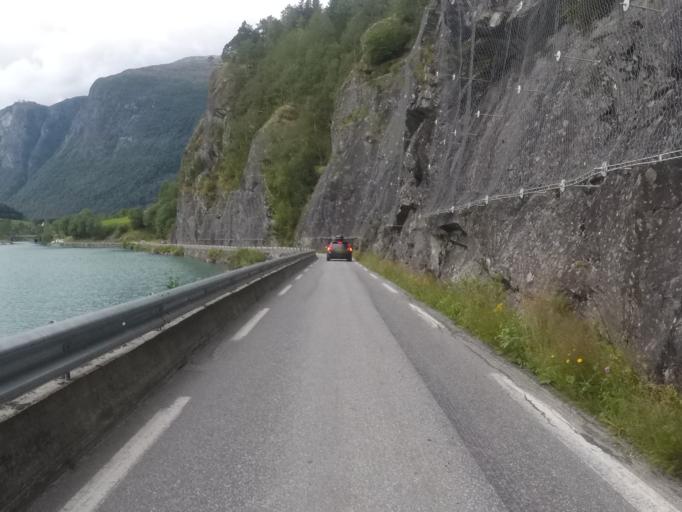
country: NO
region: Sogn og Fjordane
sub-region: Stryn
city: Stryn
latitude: 61.8574
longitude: 6.8951
